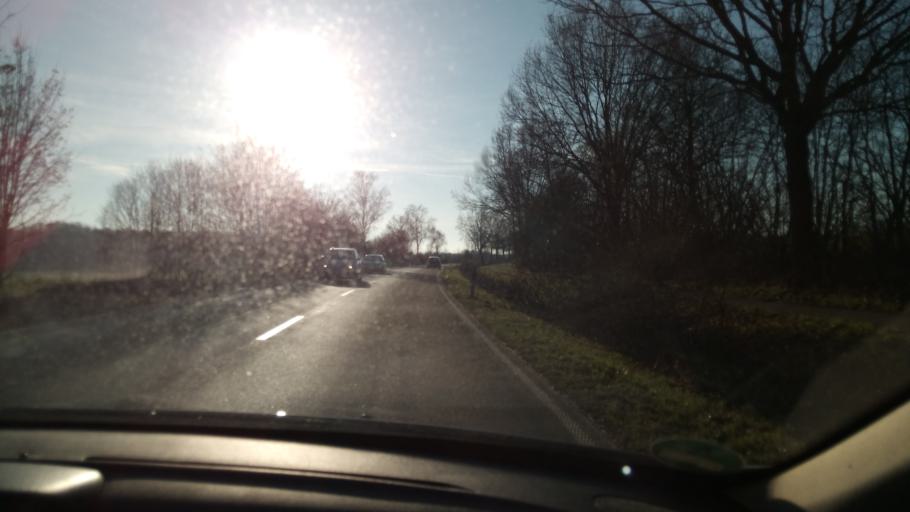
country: DE
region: Schleswig-Holstein
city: Witzeeze
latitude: 53.4597
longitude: 10.6227
